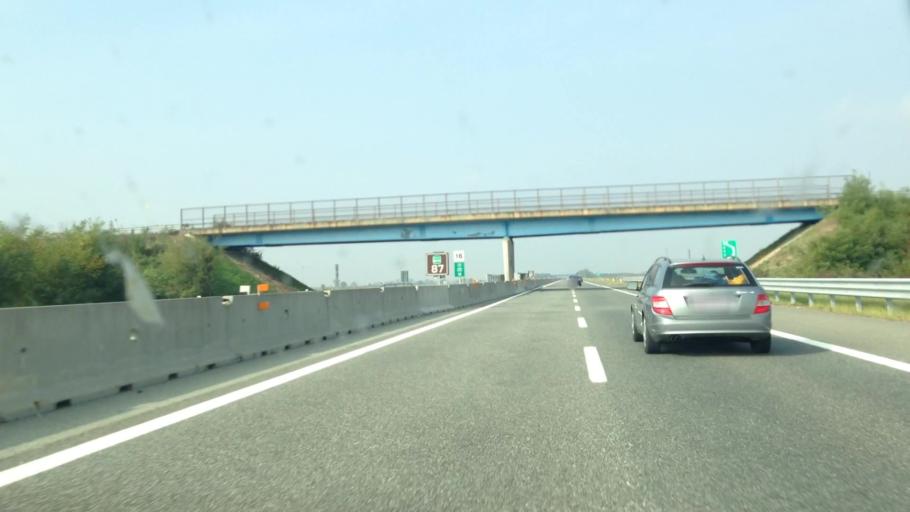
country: IT
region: Piedmont
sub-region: Provincia di Vercelli
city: Salasco
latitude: 45.3088
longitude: 8.2913
